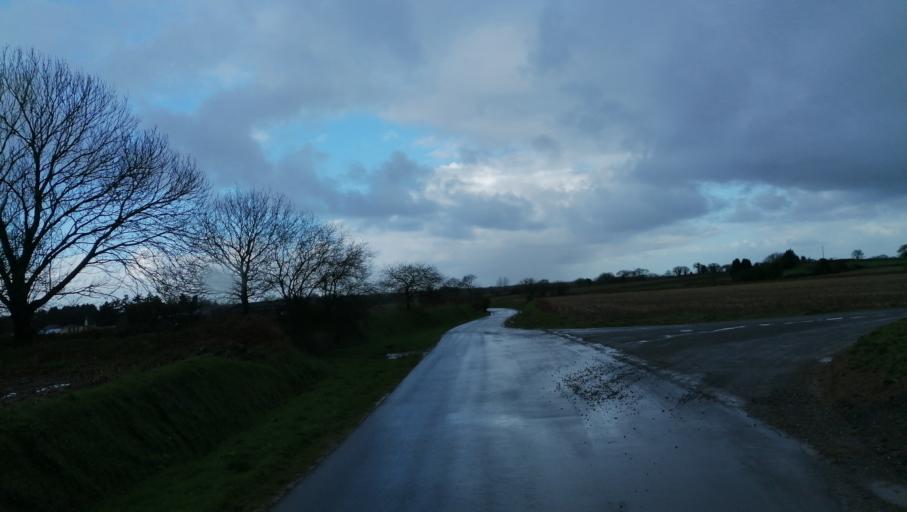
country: FR
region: Brittany
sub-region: Departement des Cotes-d'Armor
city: Lanrodec
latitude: 48.4881
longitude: -2.9971
